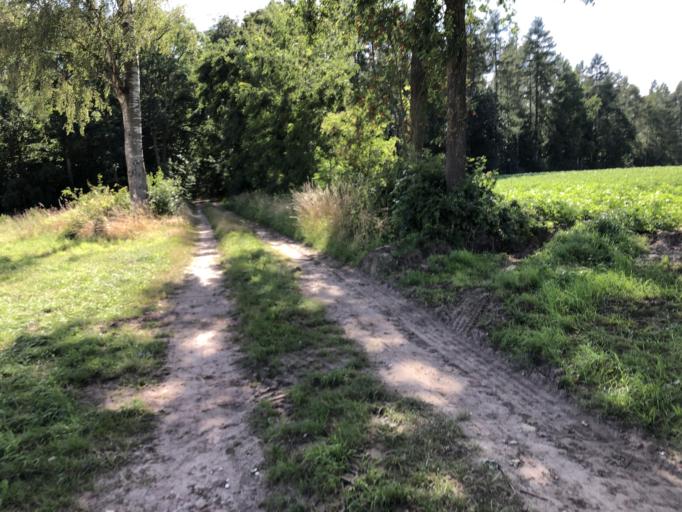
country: DE
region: Lower Saxony
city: Thomasburg
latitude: 53.1956
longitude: 10.6843
